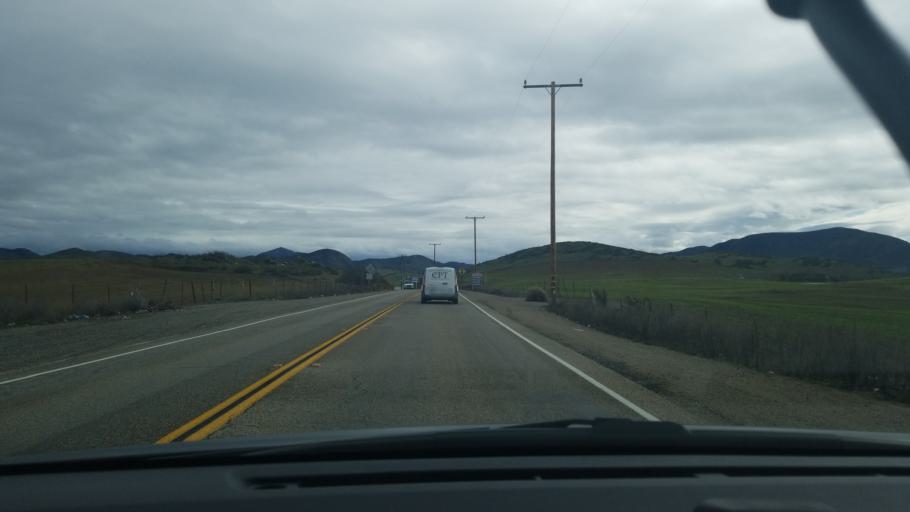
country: US
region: California
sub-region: Riverside County
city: Winchester
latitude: 33.6412
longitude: -117.0882
